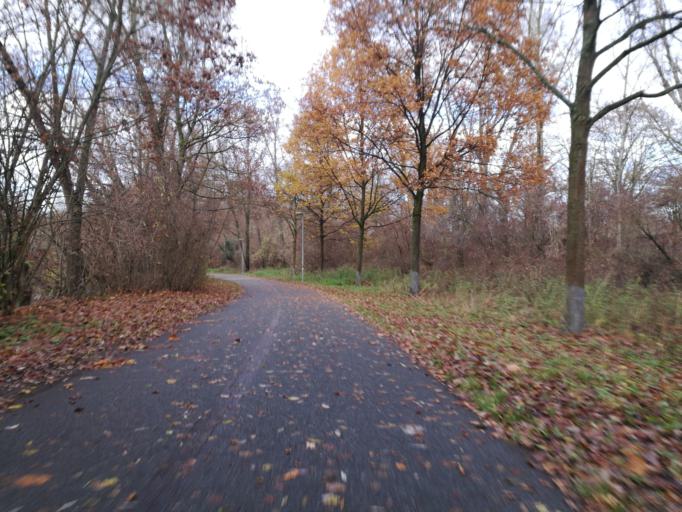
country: DE
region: Bavaria
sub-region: Regierungsbezirk Mittelfranken
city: Furth
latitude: 49.4828
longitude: 10.9928
